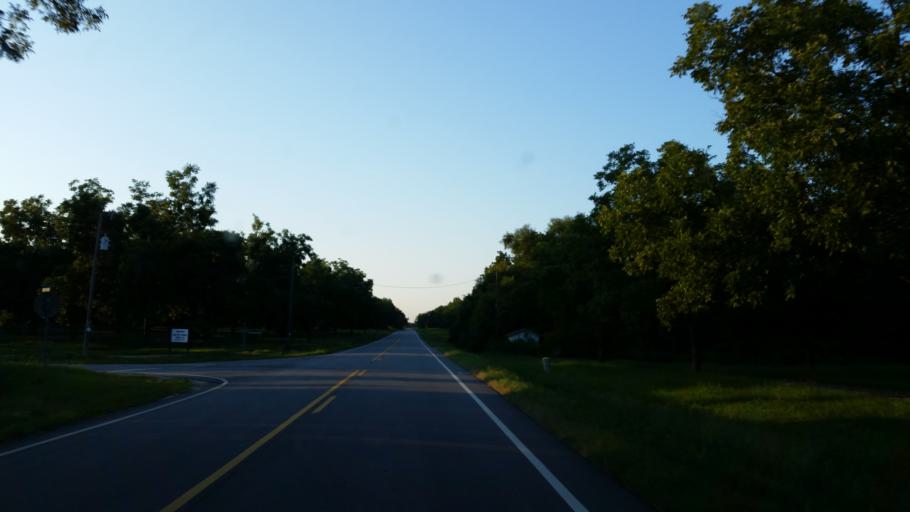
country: US
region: Georgia
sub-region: Turner County
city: Ashburn
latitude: 31.7961
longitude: -83.7097
